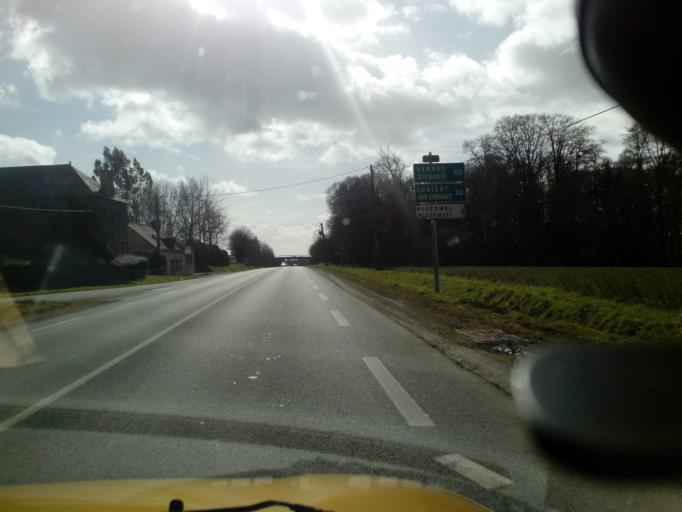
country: FR
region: Brittany
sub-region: Departement du Morbihan
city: Loyat
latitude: 47.9700
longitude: -2.3828
